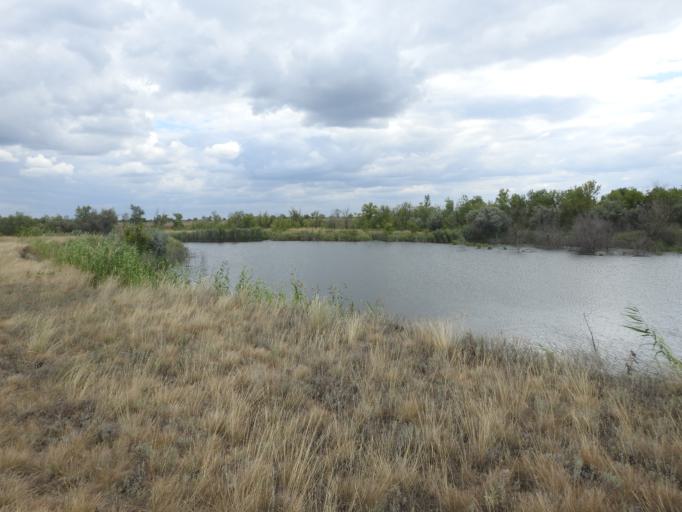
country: RU
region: Saratov
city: Shumeyka
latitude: 51.4517
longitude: 46.2670
